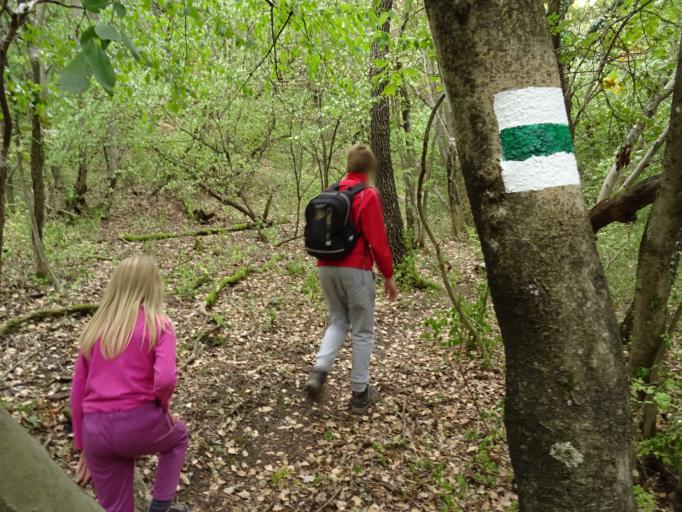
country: HU
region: Fejer
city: Kincsesbanya
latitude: 47.2302
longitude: 18.2517
